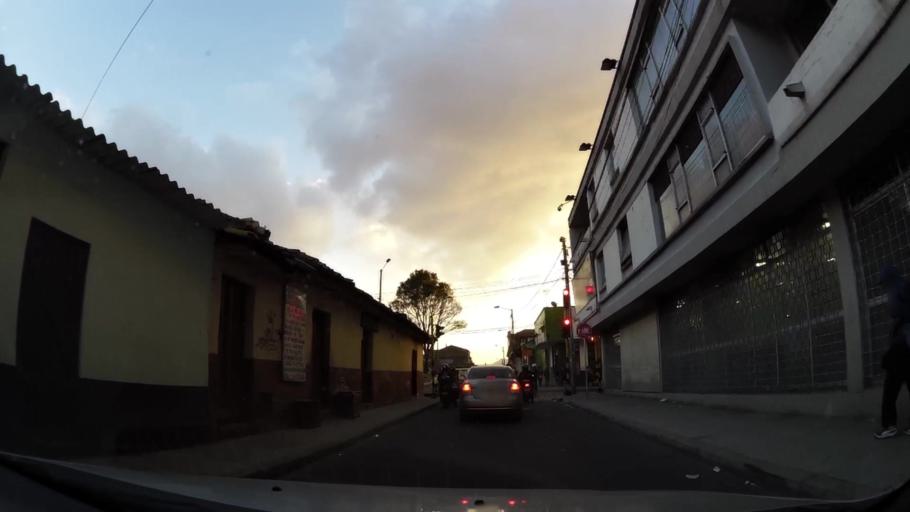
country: CO
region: Bogota D.C.
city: Bogota
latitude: 4.5900
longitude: -74.0814
